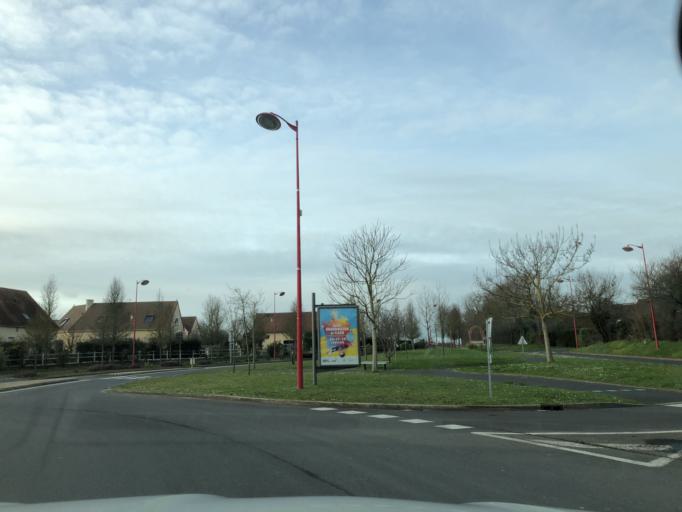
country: FR
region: Lower Normandy
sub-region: Departement du Calvados
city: Blainville-sur-Orne
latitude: 49.2315
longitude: -0.3063
